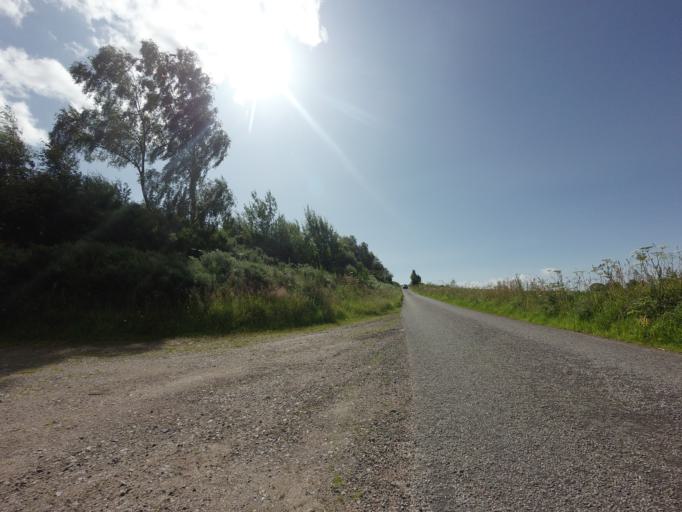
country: GB
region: Scotland
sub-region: Highland
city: Nairn
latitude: 57.5338
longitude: -3.8653
